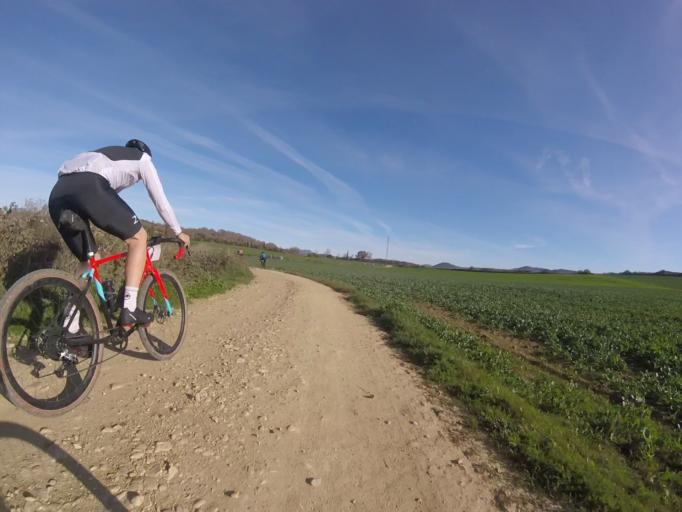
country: ES
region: Navarre
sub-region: Provincia de Navarra
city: Villatuerta
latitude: 42.6643
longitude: -1.9619
